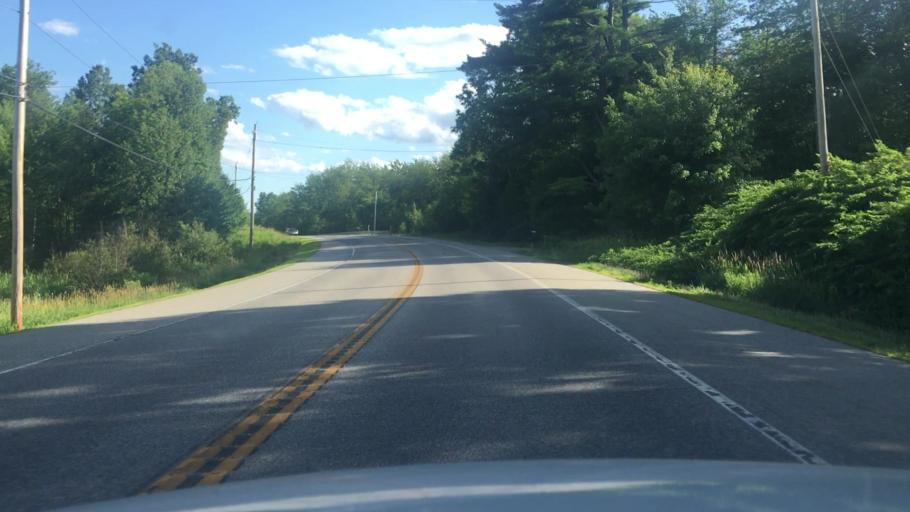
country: US
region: Maine
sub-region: Androscoggin County
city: Livermore
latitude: 44.3988
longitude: -70.2288
